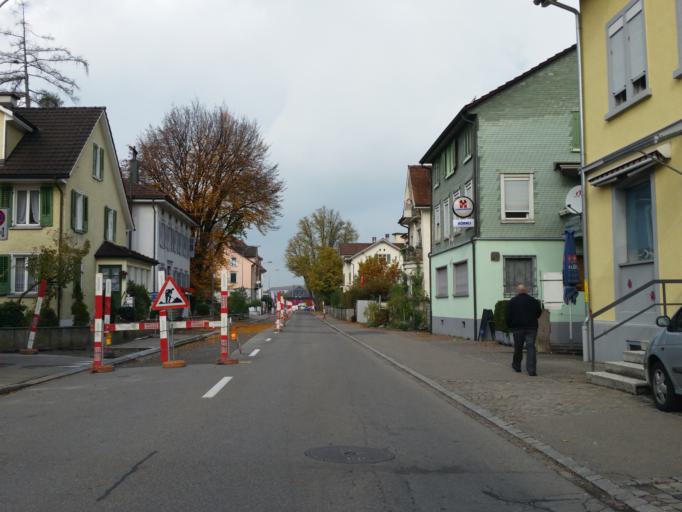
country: CH
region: Thurgau
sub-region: Arbon District
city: Amriswil
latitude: 47.5489
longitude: 9.3057
